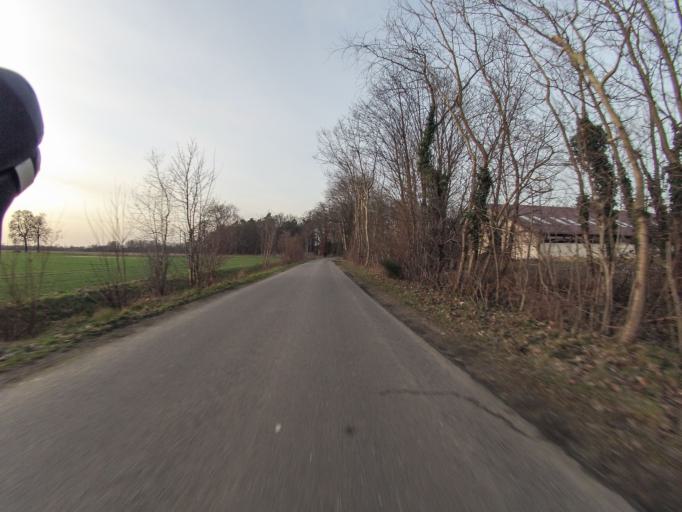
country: DE
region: North Rhine-Westphalia
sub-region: Regierungsbezirk Munster
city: Wettringen
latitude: 52.1847
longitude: 7.3309
